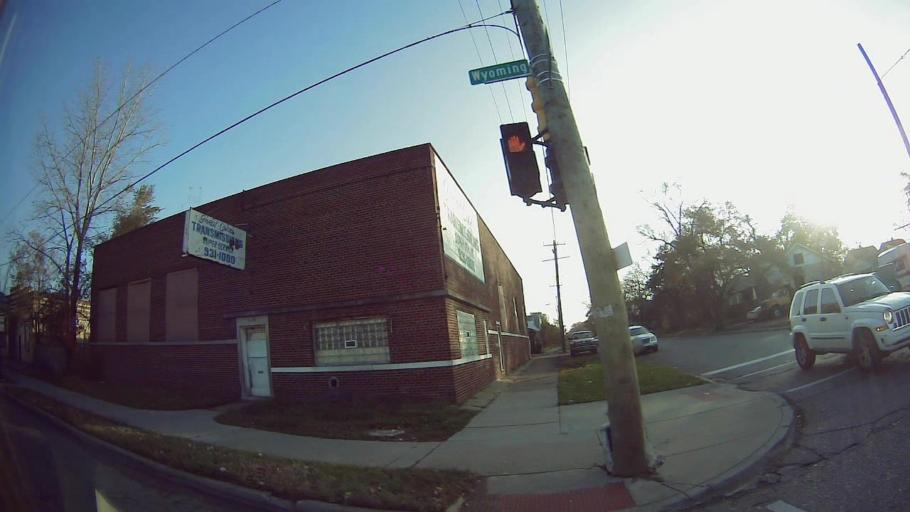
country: US
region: Michigan
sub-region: Wayne County
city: Highland Park
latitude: 42.3909
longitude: -83.1592
